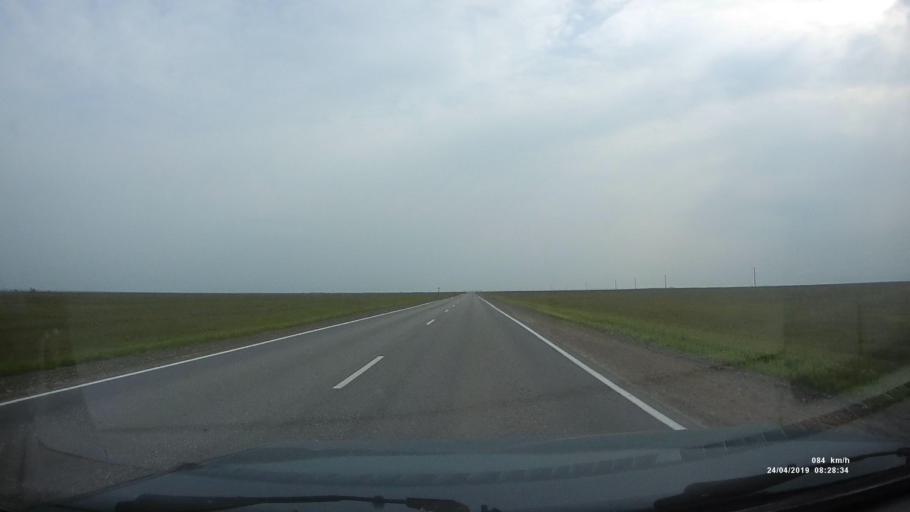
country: RU
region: Kalmykiya
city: Priyutnoye
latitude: 46.1455
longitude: 43.8177
